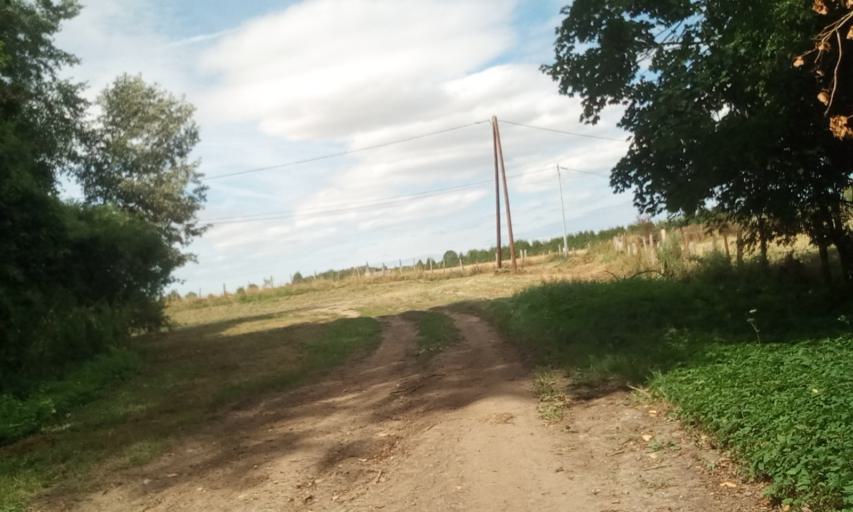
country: FR
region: Lower Normandy
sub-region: Departement du Calvados
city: Sannerville
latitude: 49.1617
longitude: -0.2152
